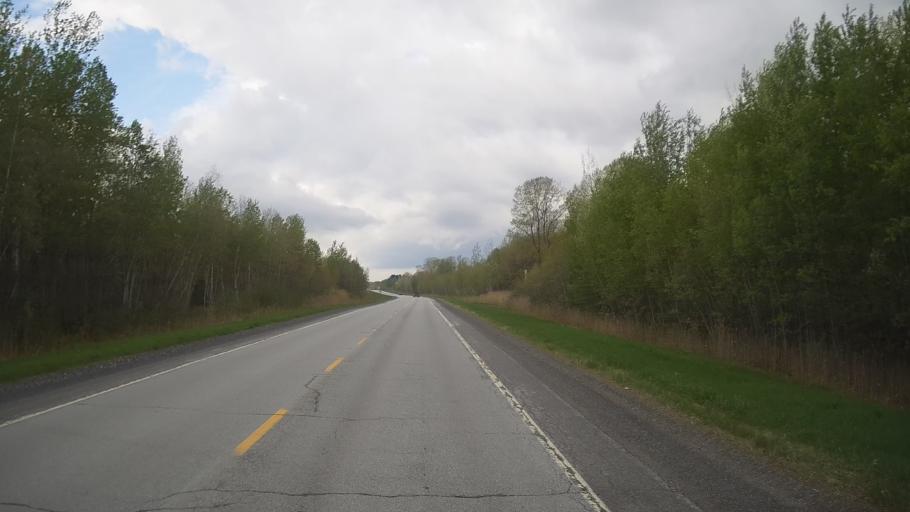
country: CA
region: Quebec
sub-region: Monteregie
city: Farnham
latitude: 45.2717
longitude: -72.9685
